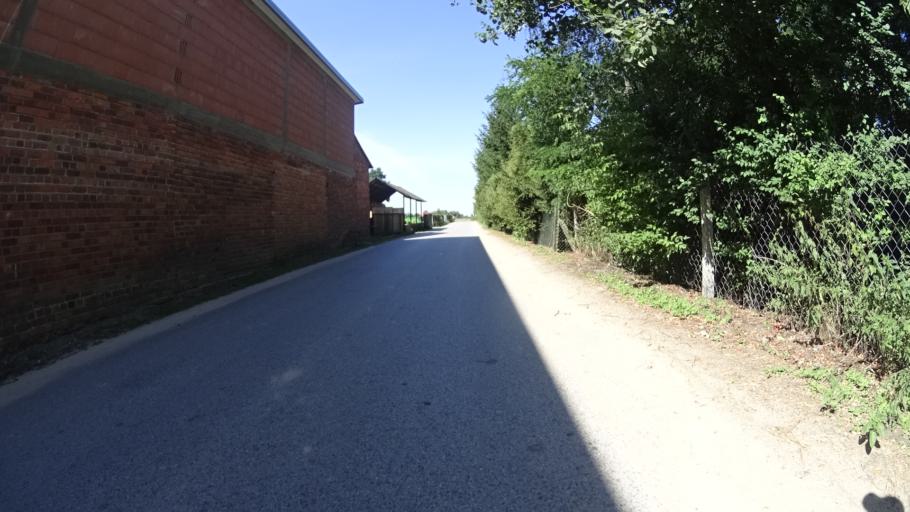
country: PL
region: Masovian Voivodeship
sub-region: Powiat bialobrzeski
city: Bialobrzegi
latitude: 51.6700
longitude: 20.9106
